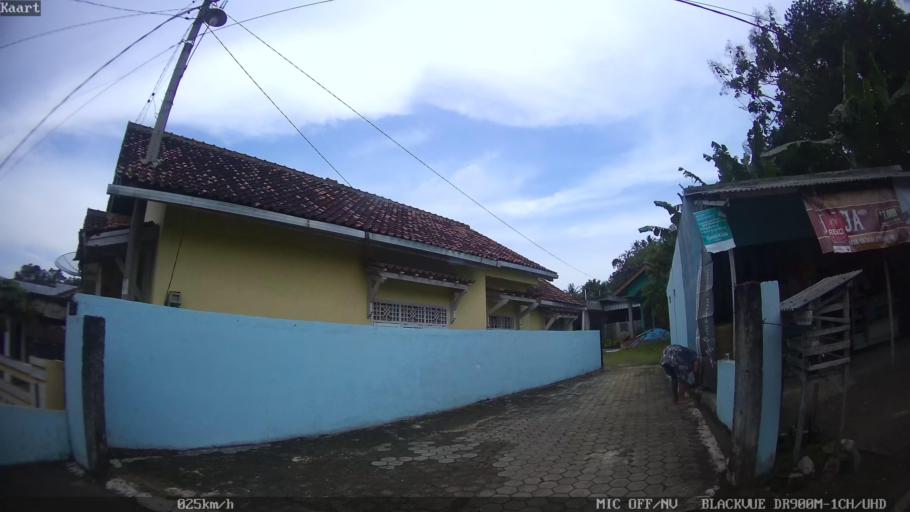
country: ID
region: Lampung
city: Kedaton
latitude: -5.3903
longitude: 105.1966
